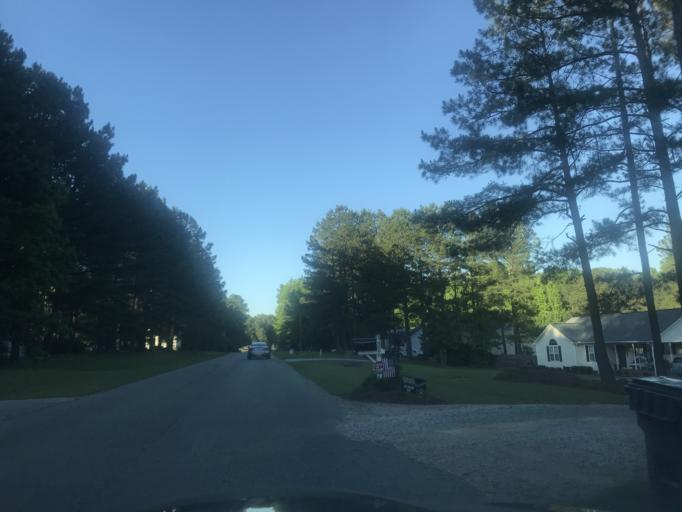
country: US
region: North Carolina
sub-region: Johnston County
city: Archer Lodge
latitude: 35.6843
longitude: -78.3479
